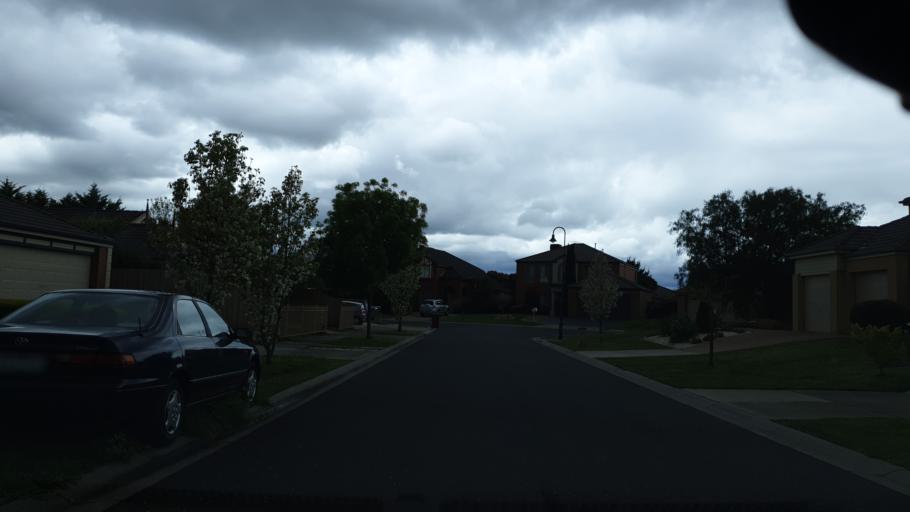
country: AU
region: Victoria
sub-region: Casey
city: Cranbourne North
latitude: -38.0662
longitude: 145.2884
